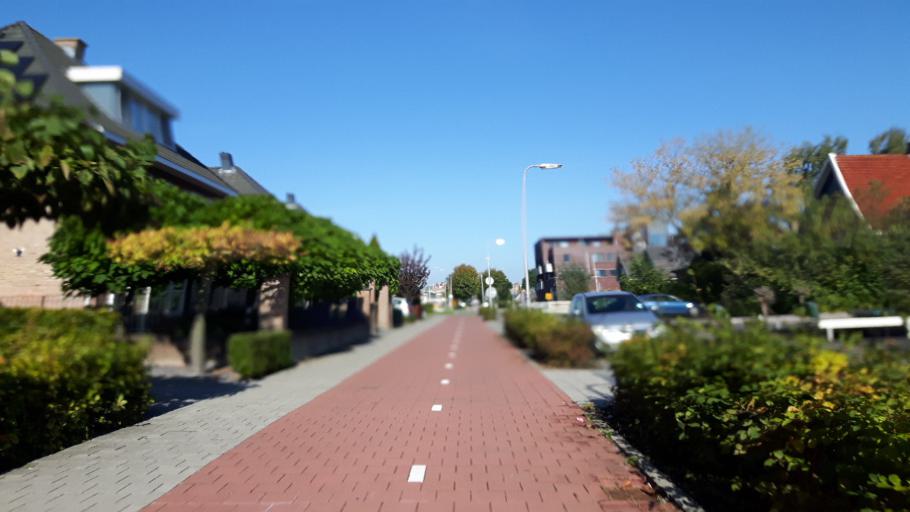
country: NL
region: South Holland
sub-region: Molenwaard
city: Liesveld
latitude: 51.9292
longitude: 4.7856
